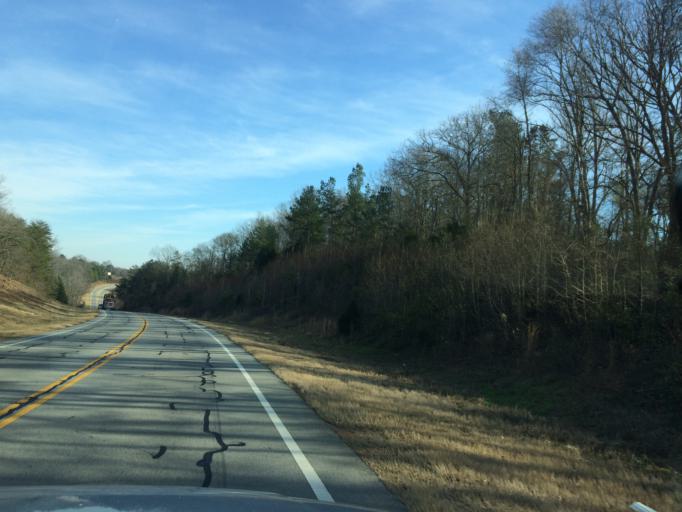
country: US
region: Georgia
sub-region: Franklin County
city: Lavonia
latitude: 34.4532
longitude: -83.0463
